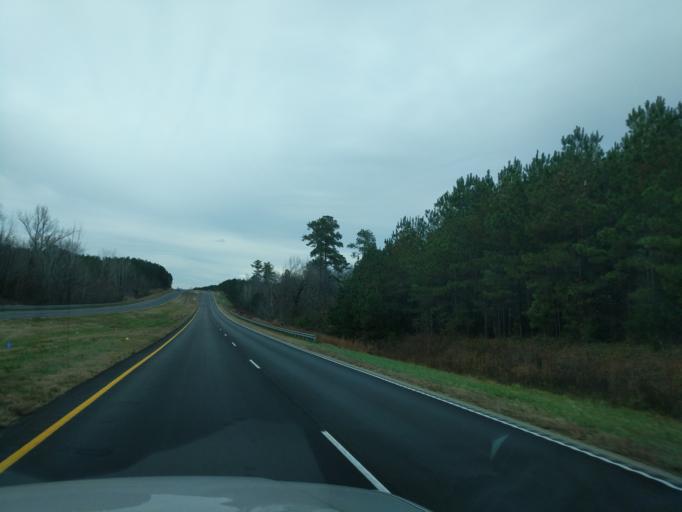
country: US
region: South Carolina
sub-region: Laurens County
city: Clinton
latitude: 34.3742
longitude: -81.9570
